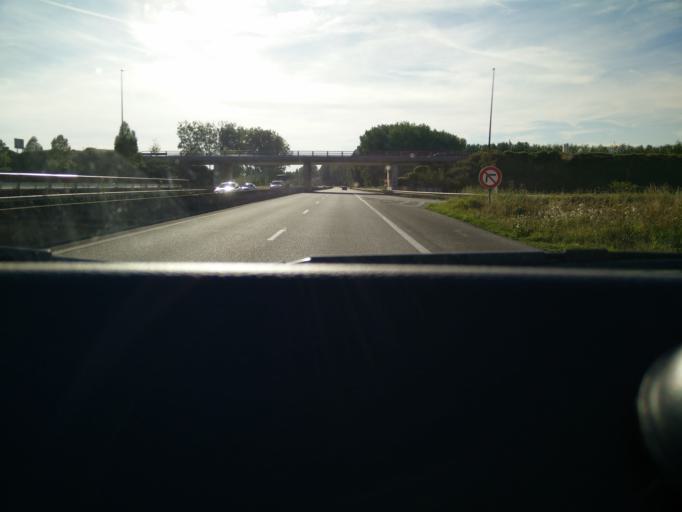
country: FR
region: Nord-Pas-de-Calais
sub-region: Departement du Nord
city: Pecquencourt
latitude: 50.3820
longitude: 3.2218
